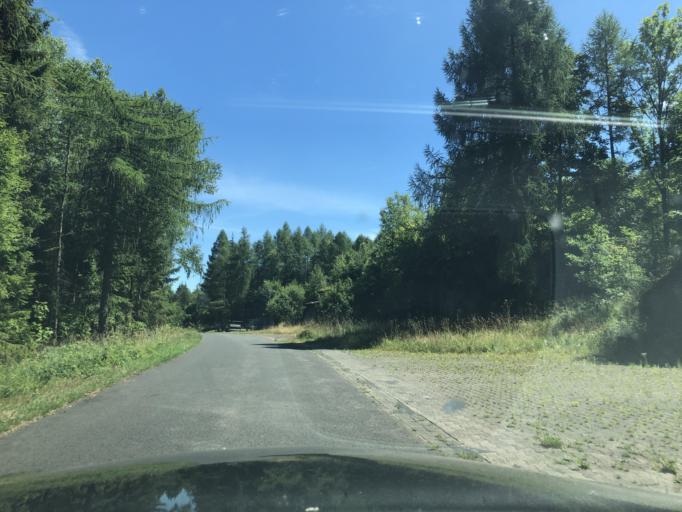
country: DE
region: Hesse
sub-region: Regierungsbezirk Giessen
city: Grebenhain
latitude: 50.5002
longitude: 9.2896
